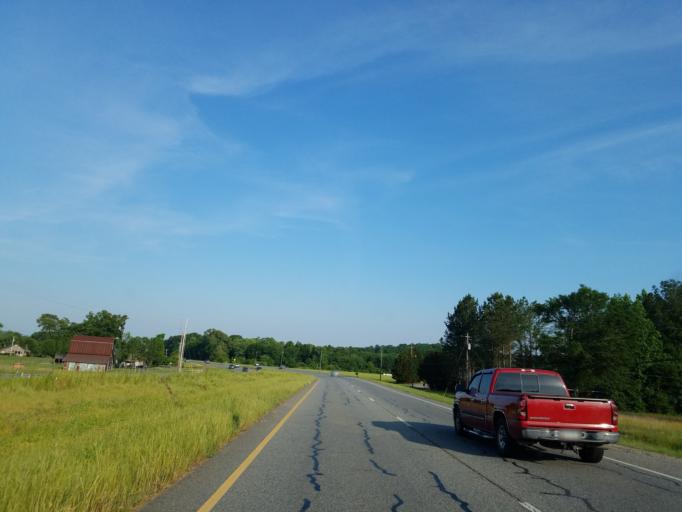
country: US
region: Georgia
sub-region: Floyd County
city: Shannon
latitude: 34.3971
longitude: -85.2032
